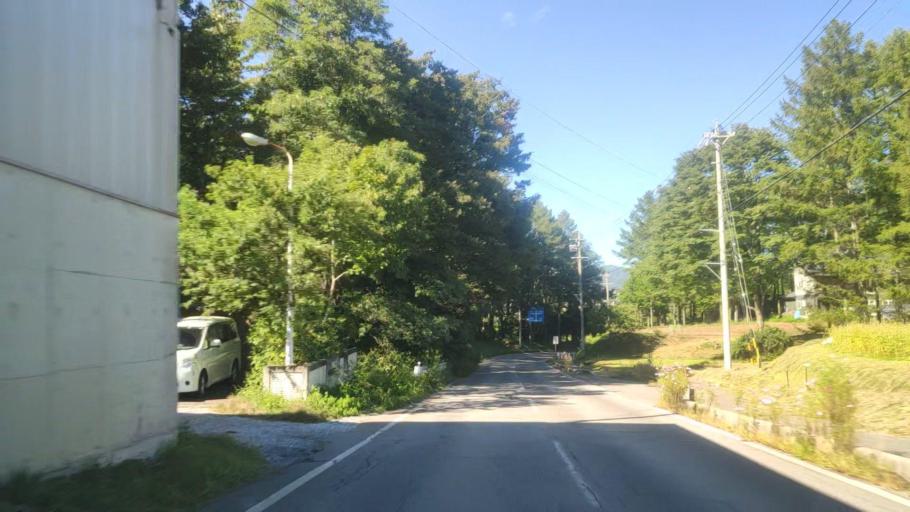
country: JP
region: Nagano
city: Chino
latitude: 36.0086
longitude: 138.2088
